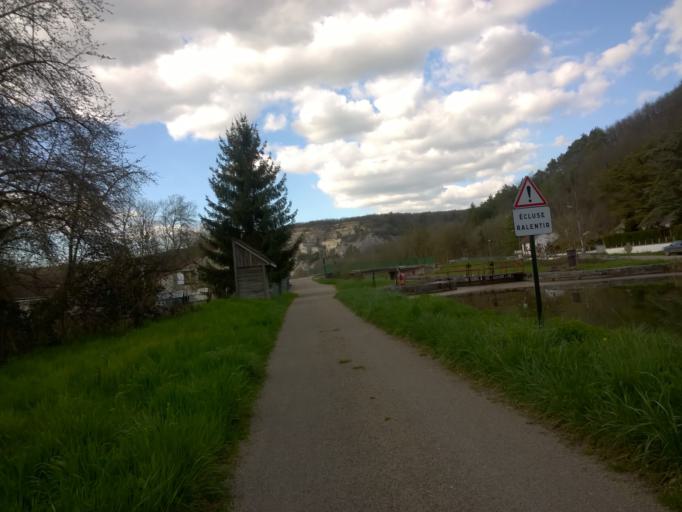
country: FR
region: Bourgogne
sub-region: Departement de l'Yonne
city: Ravieres
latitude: 47.7059
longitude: 4.2444
